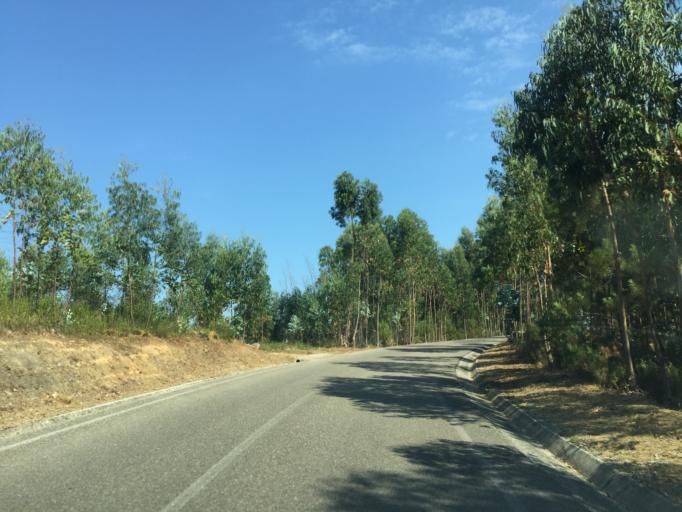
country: PT
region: Santarem
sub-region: Ferreira do Zezere
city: Ferreira do Zezere
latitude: 39.5891
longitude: -8.2991
